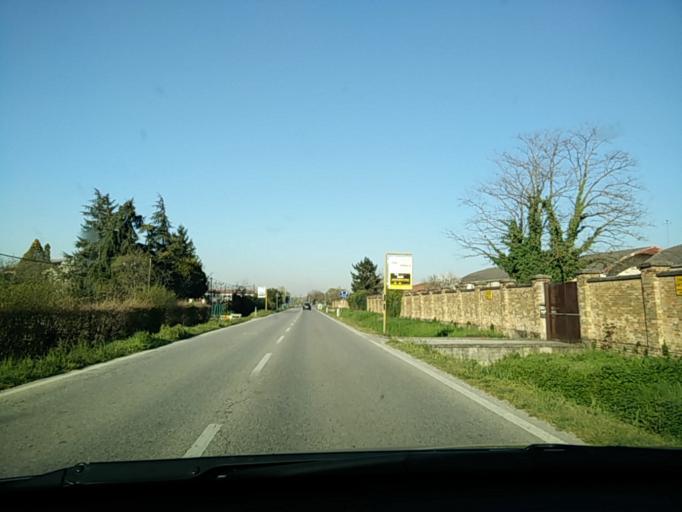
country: IT
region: Veneto
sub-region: Provincia di Venezia
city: Campalto
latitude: 45.4907
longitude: 12.3046
